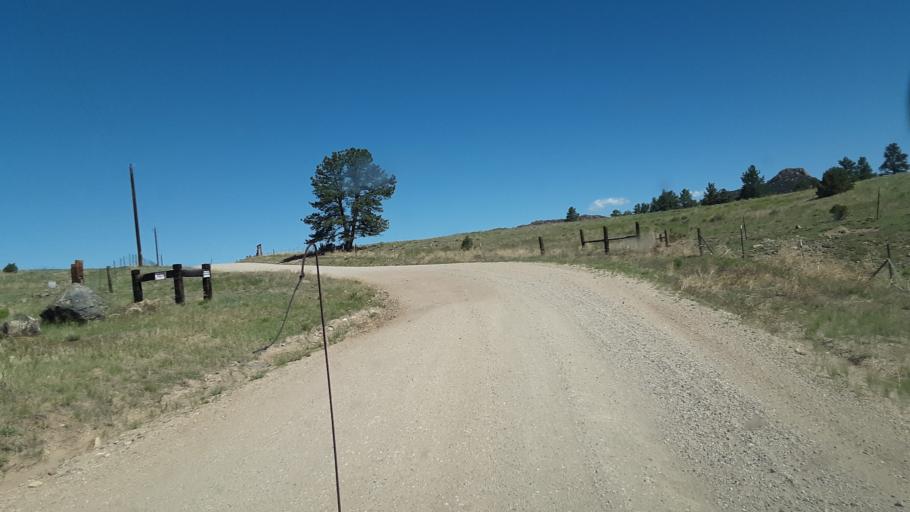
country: US
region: Colorado
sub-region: Custer County
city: Westcliffe
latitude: 38.2142
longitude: -105.4457
